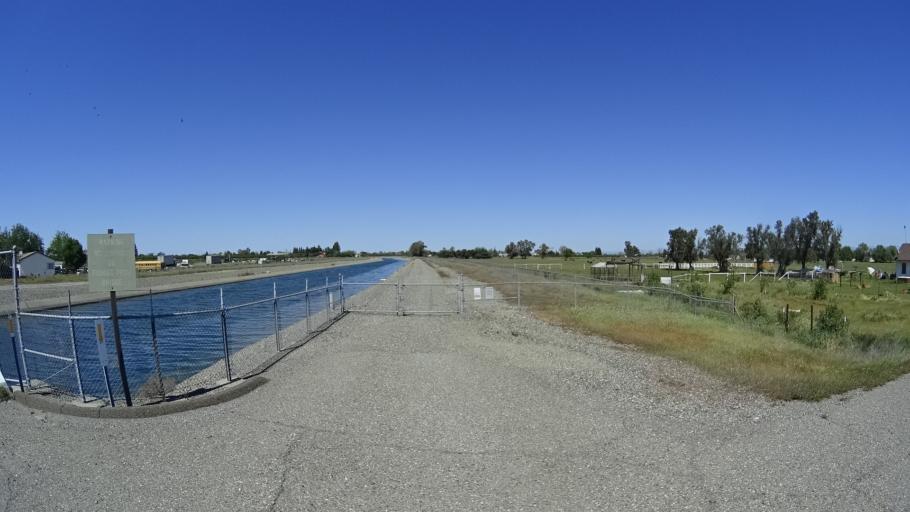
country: US
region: California
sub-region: Glenn County
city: Orland
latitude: 39.7397
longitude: -122.1543
